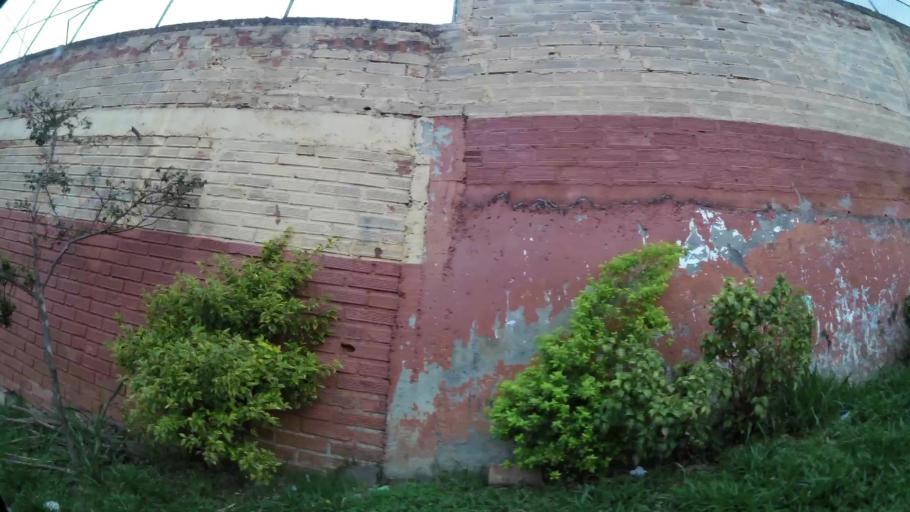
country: CO
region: Antioquia
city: Medellin
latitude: 6.2895
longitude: -75.5503
